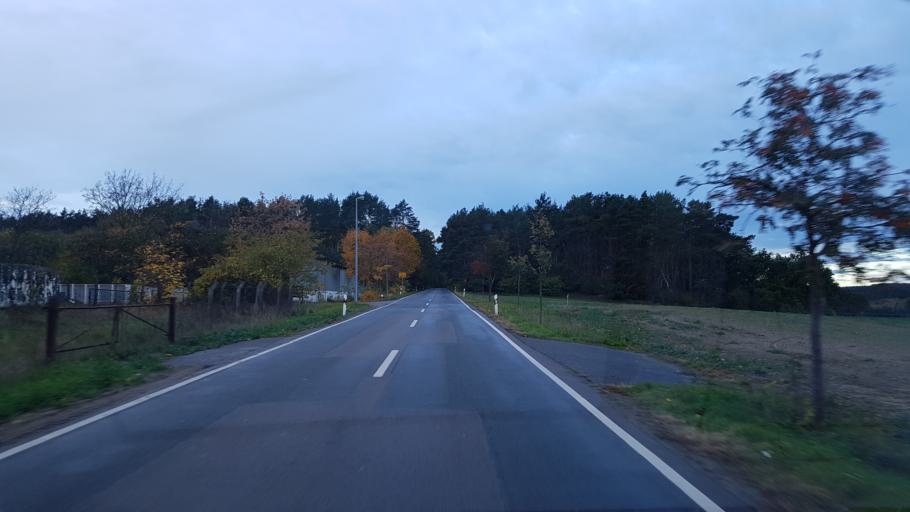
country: DE
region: Saxony
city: Belgern
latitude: 51.4468
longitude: 13.1088
